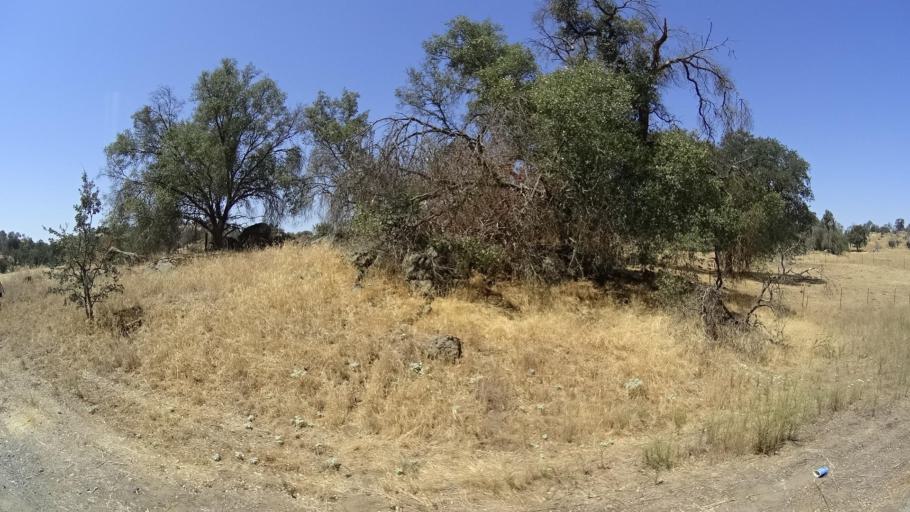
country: US
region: California
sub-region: Mariposa County
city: Mariposa
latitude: 37.3001
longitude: -119.9760
